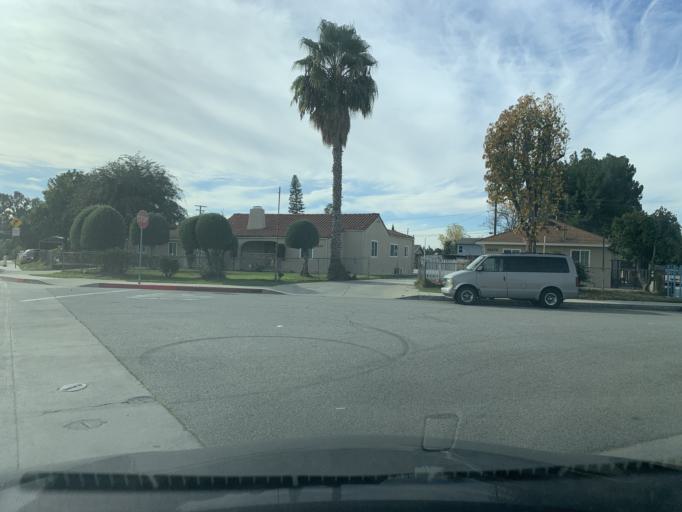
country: US
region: California
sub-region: Los Angeles County
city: El Monte
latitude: 34.0745
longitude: -118.0465
